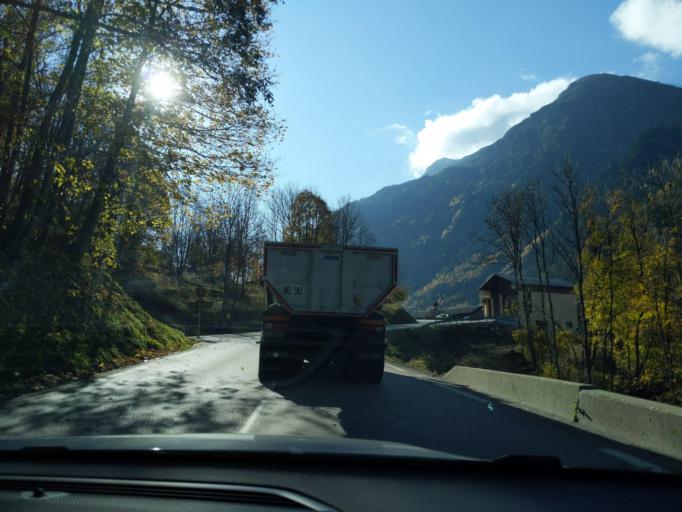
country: FR
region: Rhone-Alpes
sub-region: Departement de la Savoie
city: Tignes
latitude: 45.5759
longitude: 6.8844
